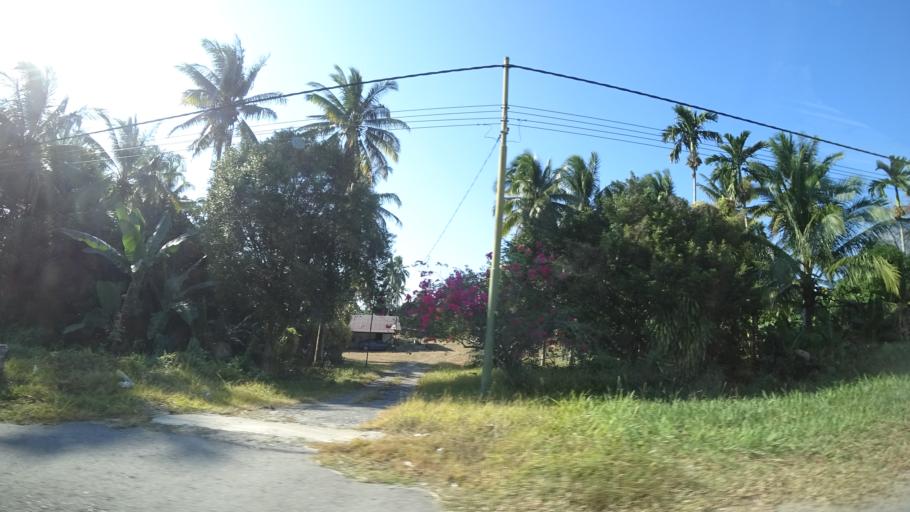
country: BN
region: Tutong
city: Tutong
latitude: 4.6880
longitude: 114.5094
